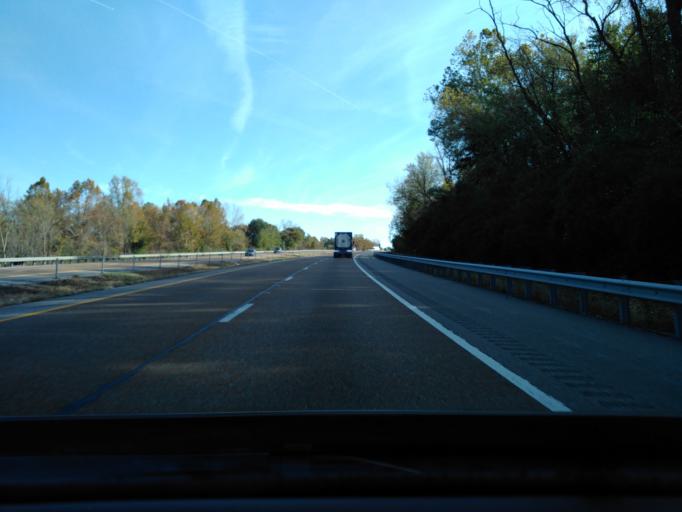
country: US
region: Illinois
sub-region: Madison County
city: Collinsville
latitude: 38.7008
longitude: -89.9891
